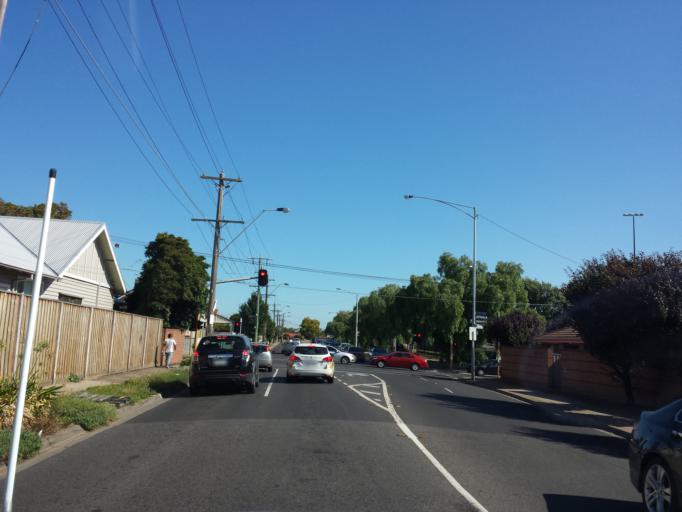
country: AU
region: Victoria
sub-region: Moonee Valley
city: Moonee Ponds
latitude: -37.7647
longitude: 144.9059
